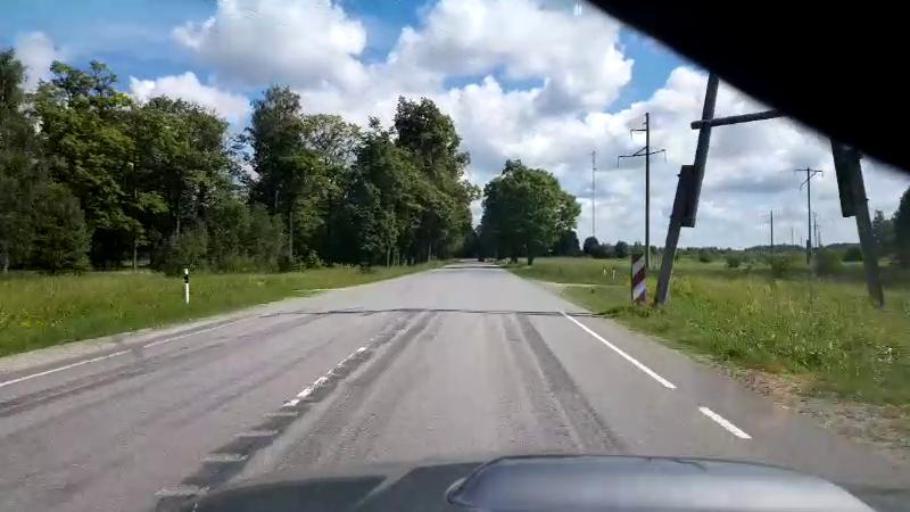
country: EE
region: Laeaene-Virumaa
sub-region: Tapa vald
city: Tapa
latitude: 59.2473
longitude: 25.9323
